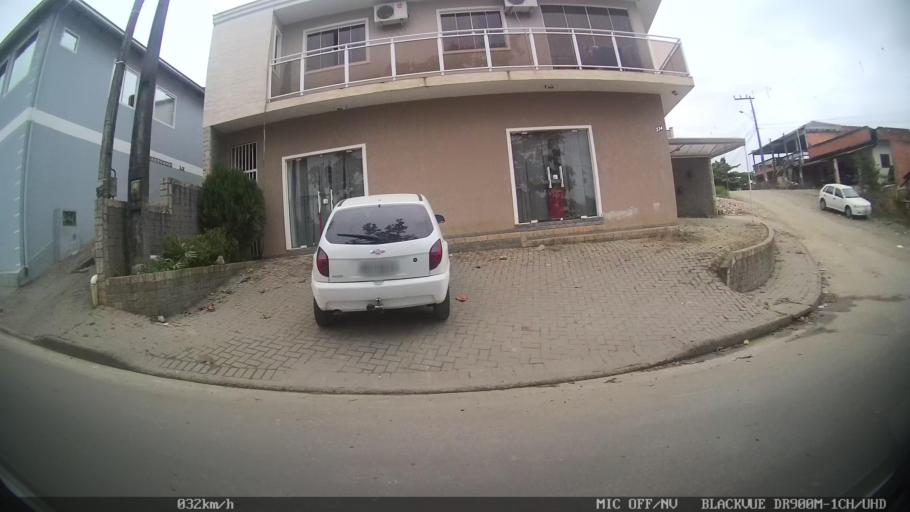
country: BR
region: Santa Catarina
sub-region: Joinville
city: Joinville
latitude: -26.3494
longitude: -48.8259
